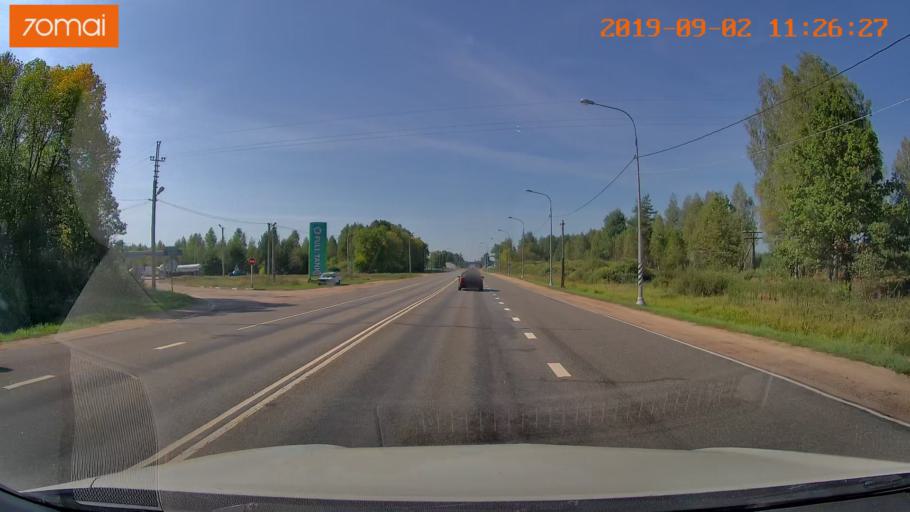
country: RU
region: Smolensk
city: Roslavl'
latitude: 53.9925
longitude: 32.9312
